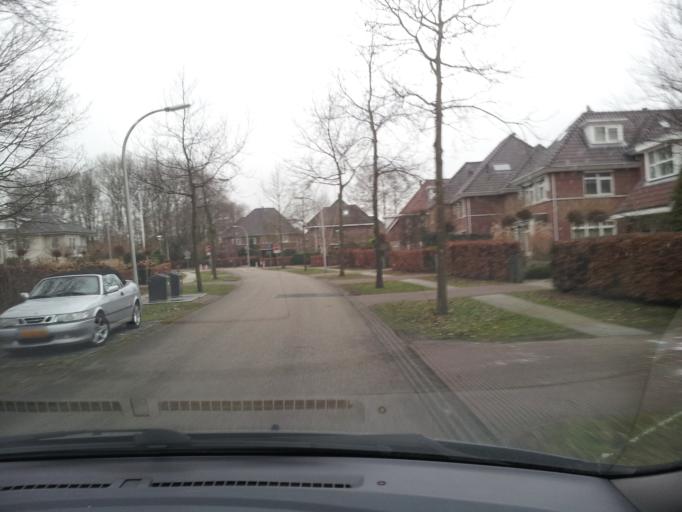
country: NL
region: South Holland
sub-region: Gemeente Den Haag
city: Ypenburg
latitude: 52.0489
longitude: 4.3679
